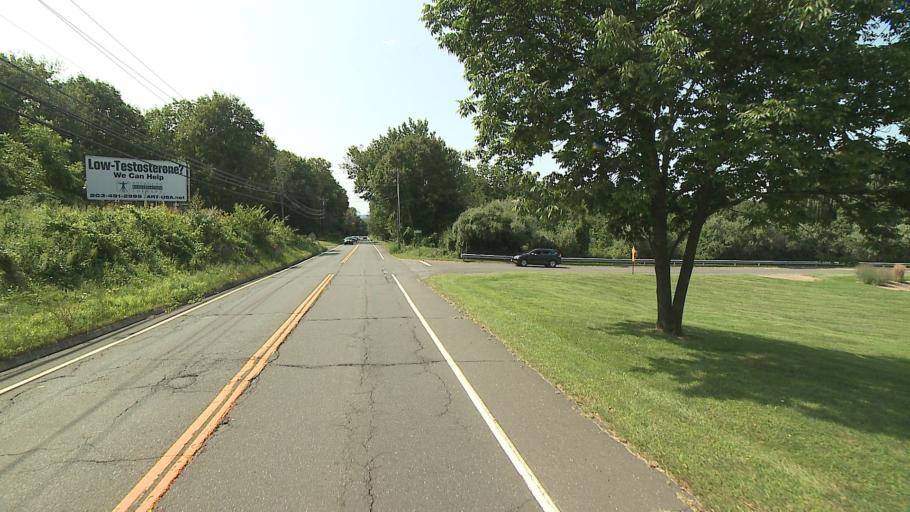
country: US
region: Connecticut
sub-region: Fairfield County
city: Newtown
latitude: 41.4192
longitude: -73.3394
